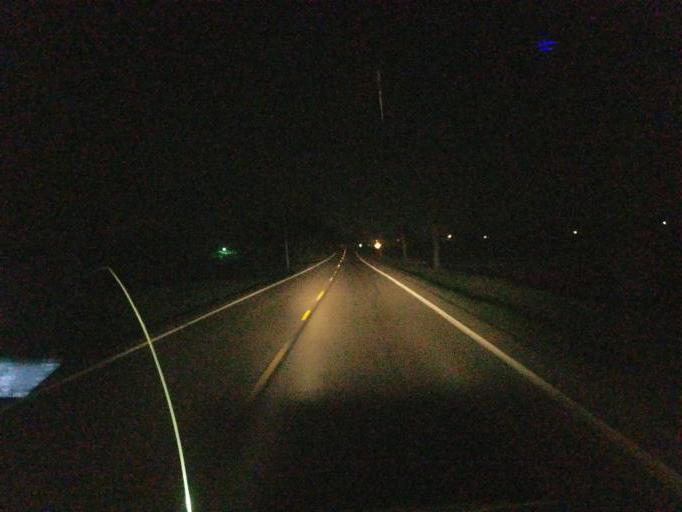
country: US
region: Ohio
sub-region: Huron County
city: Monroeville
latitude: 41.2802
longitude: -82.7208
